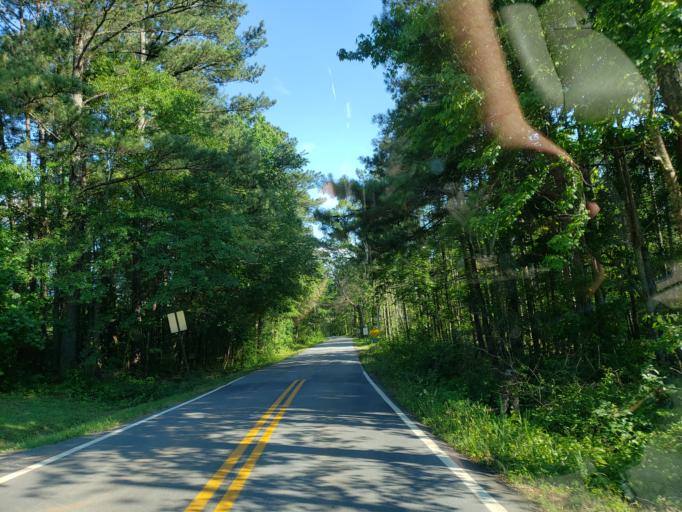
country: US
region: Georgia
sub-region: Haralson County
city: Bremen
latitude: 33.6998
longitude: -85.1006
